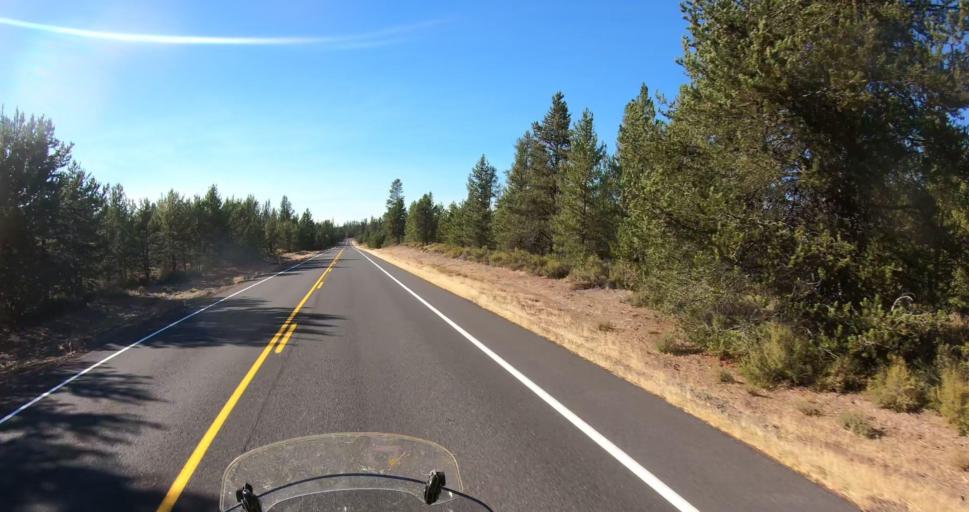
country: US
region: Oregon
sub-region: Deschutes County
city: La Pine
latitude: 43.4530
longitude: -121.3686
